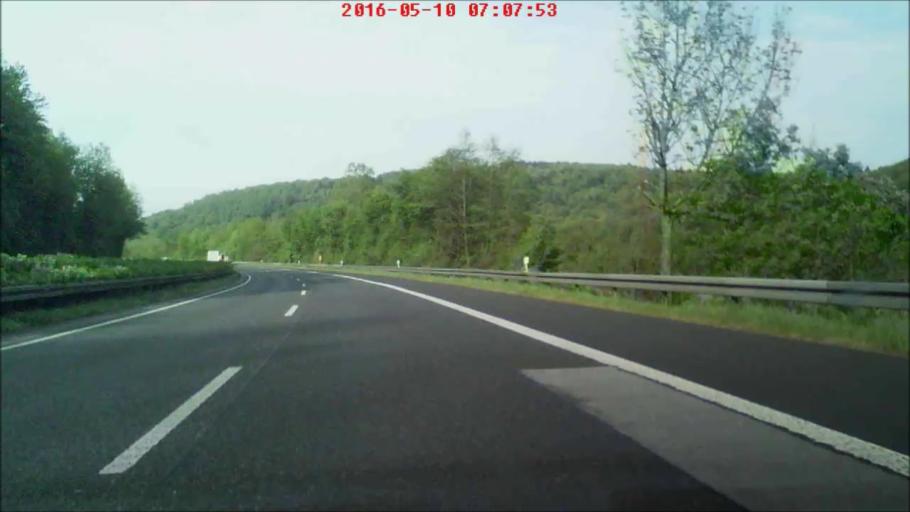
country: DE
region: Hesse
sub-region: Regierungsbezirk Darmstadt
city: Wachtersbach
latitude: 50.2236
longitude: 9.2487
